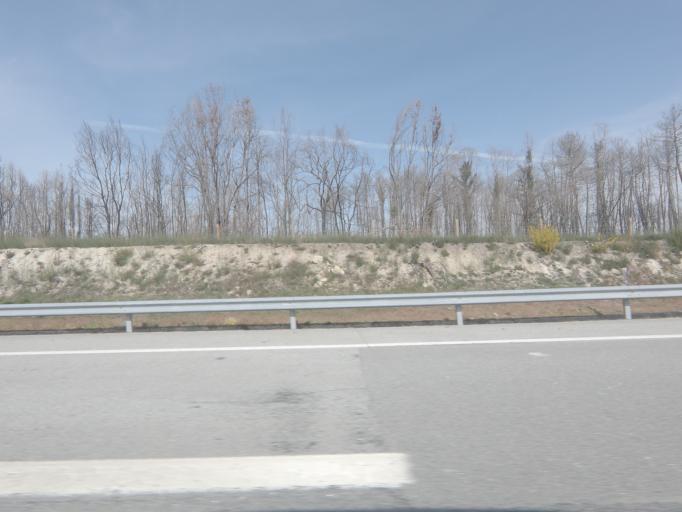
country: PT
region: Viseu
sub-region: Oliveira de Frades
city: Oliveira de Frades
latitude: 40.6843
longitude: -8.2038
